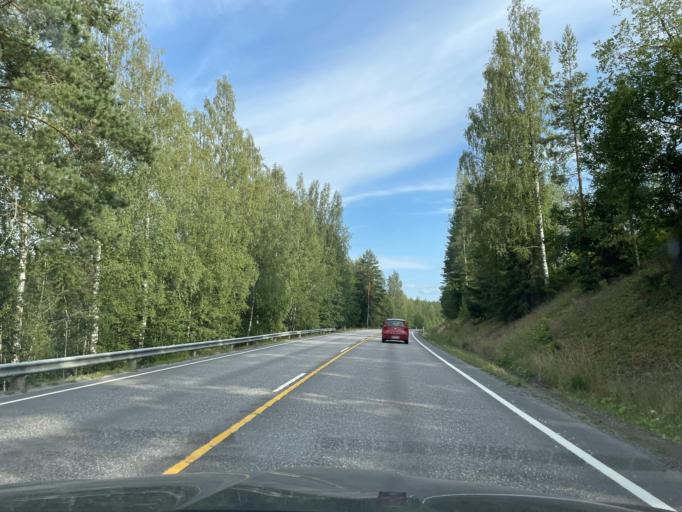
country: FI
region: Central Finland
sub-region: Jaemsae
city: Kuhmoinen
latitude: 61.4385
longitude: 25.1815
